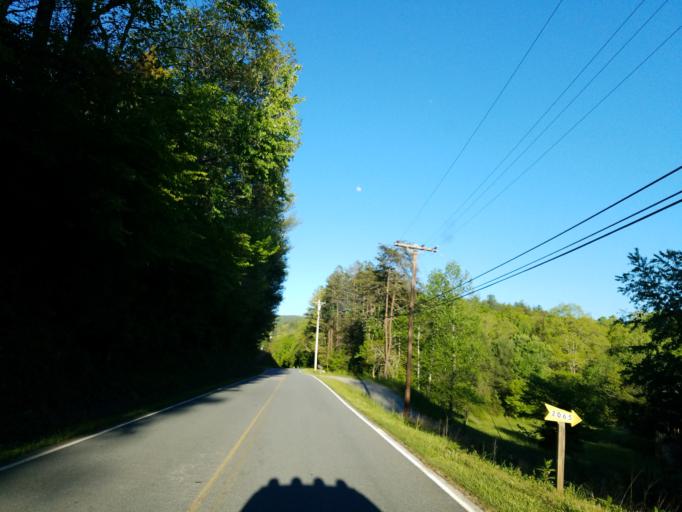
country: US
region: Georgia
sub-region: Fannin County
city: Blue Ridge
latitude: 34.7584
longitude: -84.2118
